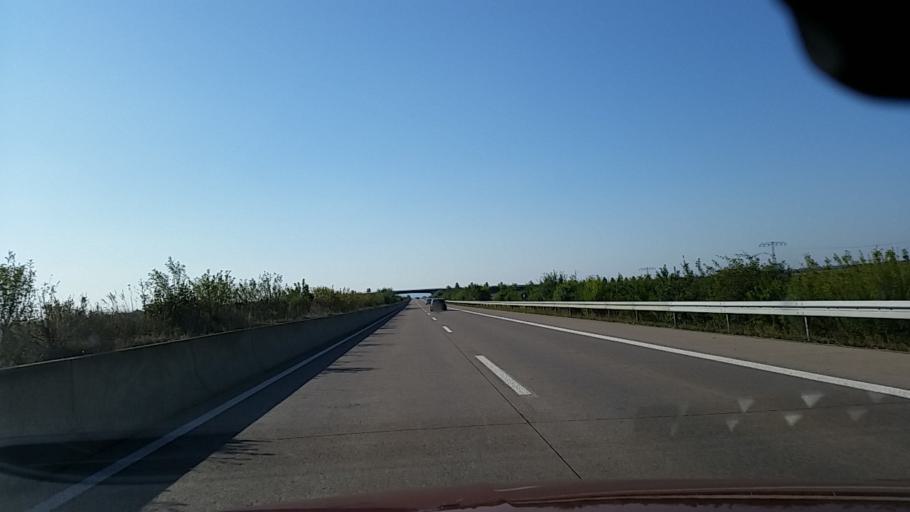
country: DE
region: Thuringia
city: Schlossvippach
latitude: 51.0977
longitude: 11.1255
